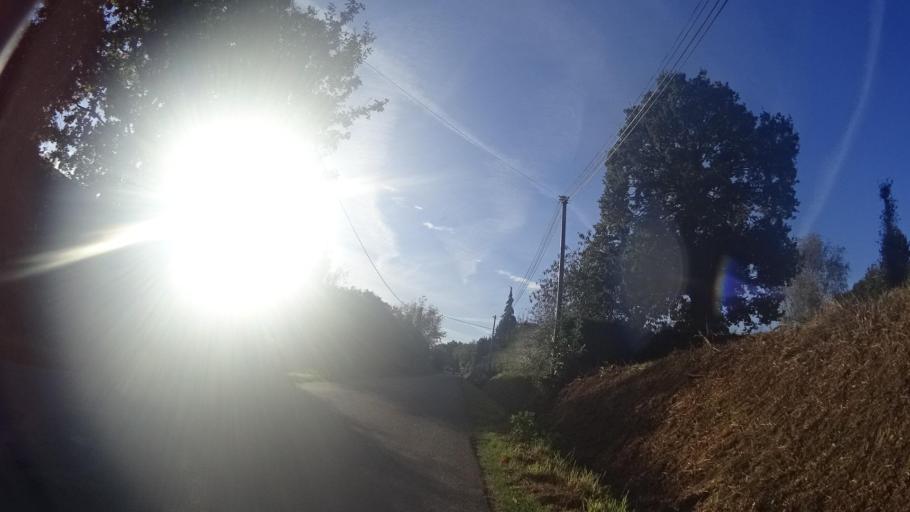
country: FR
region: Brittany
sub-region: Departement des Cotes-d'Armor
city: Evran
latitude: 48.3394
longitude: -1.9378
